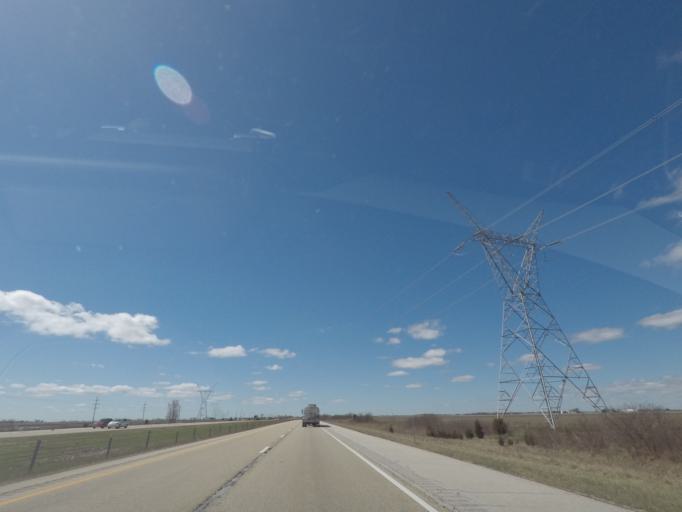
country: US
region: Illinois
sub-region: Livingston County
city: Dwight
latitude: 41.1376
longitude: -88.3728
